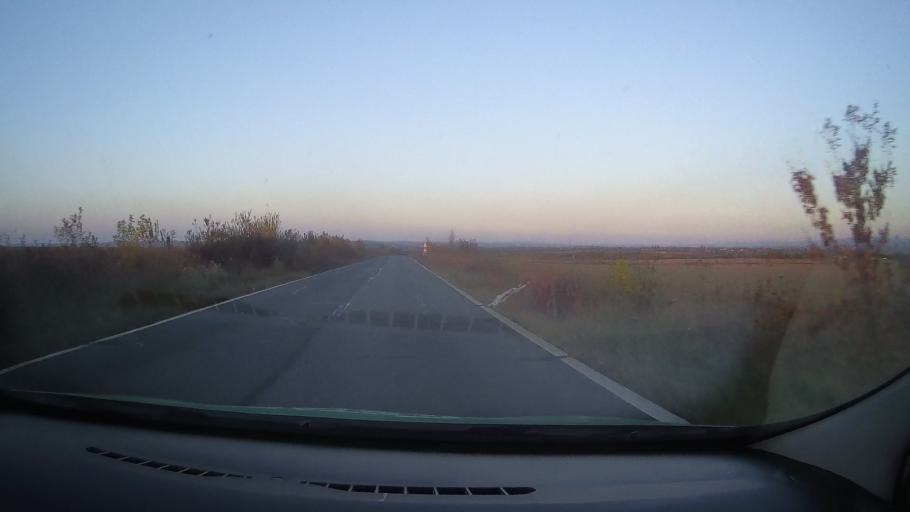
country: RO
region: Timis
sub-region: Comuna Manastiur
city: Manastiur
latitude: 45.8226
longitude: 22.0856
